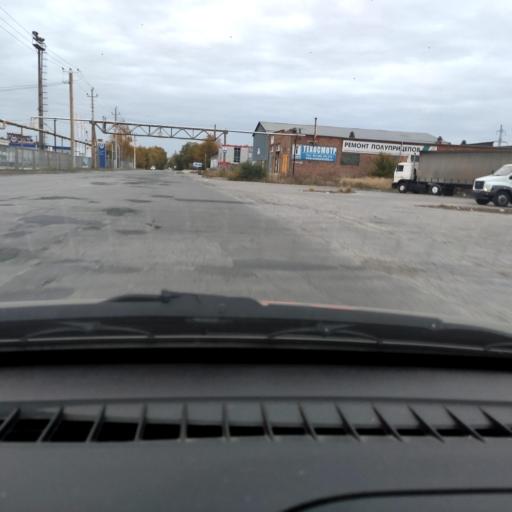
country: RU
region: Samara
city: Tol'yatti
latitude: 53.5711
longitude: 49.2875
